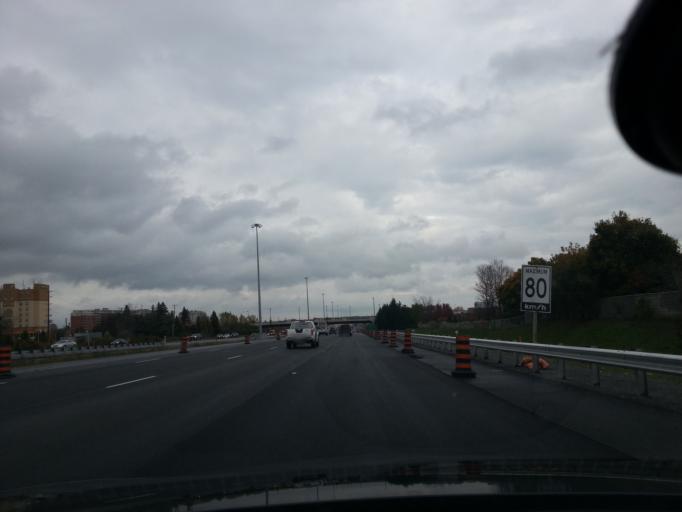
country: CA
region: Ontario
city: Bells Corners
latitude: 45.3086
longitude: -75.9060
